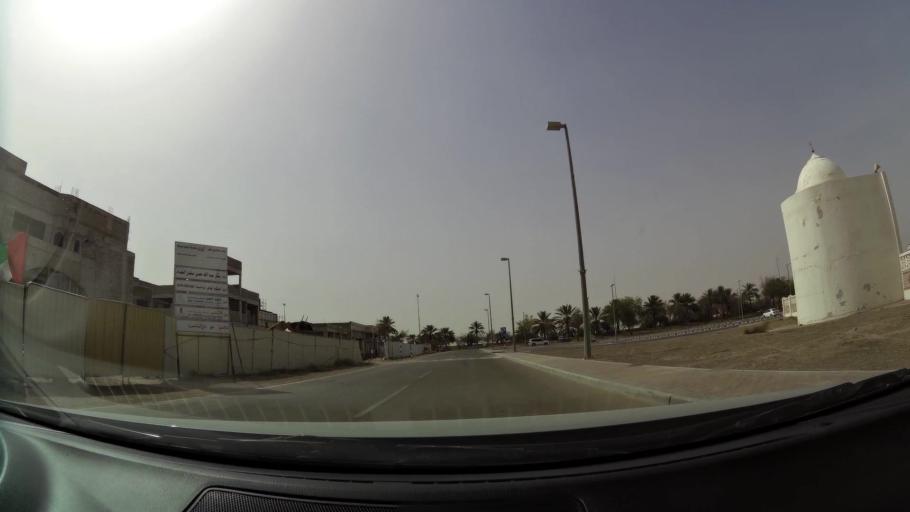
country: AE
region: Abu Dhabi
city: Al Ain
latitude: 24.1959
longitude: 55.6330
